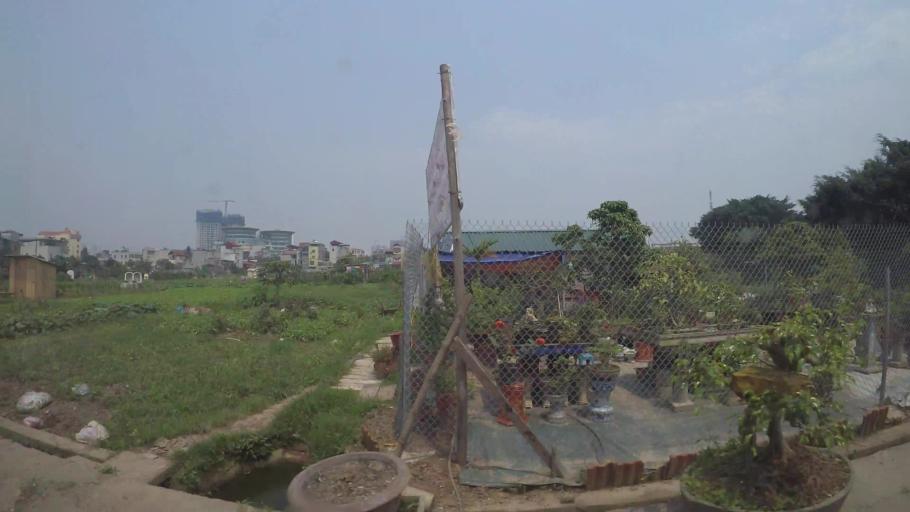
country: VN
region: Ha Noi
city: Van Dien
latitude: 20.9476
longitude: 105.8420
